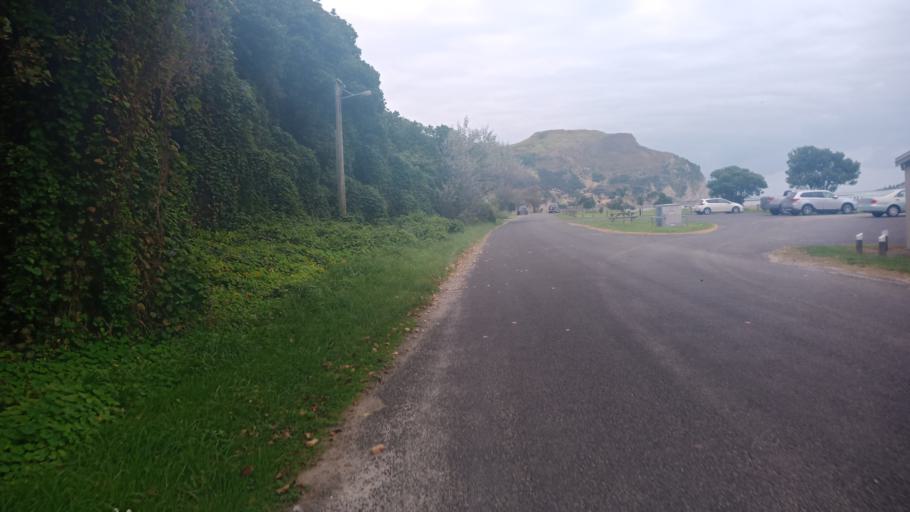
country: NZ
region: Gisborne
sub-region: Gisborne District
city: Gisborne
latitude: -38.6822
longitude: 178.0311
